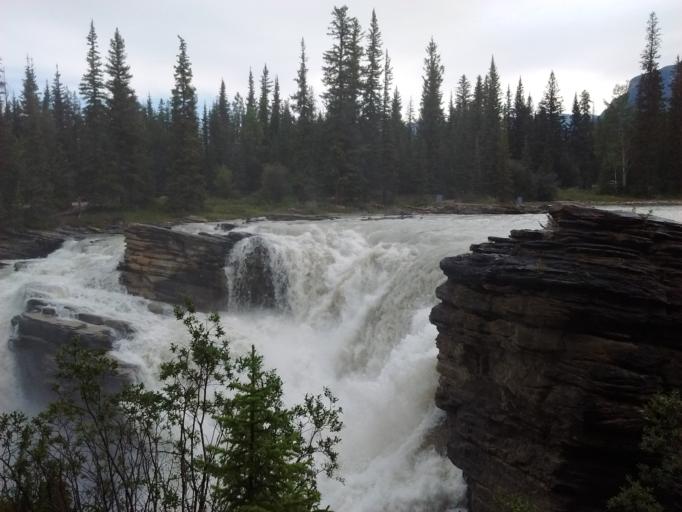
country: CA
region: Alberta
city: Jasper Park Lodge
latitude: 52.6643
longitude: -117.8836
